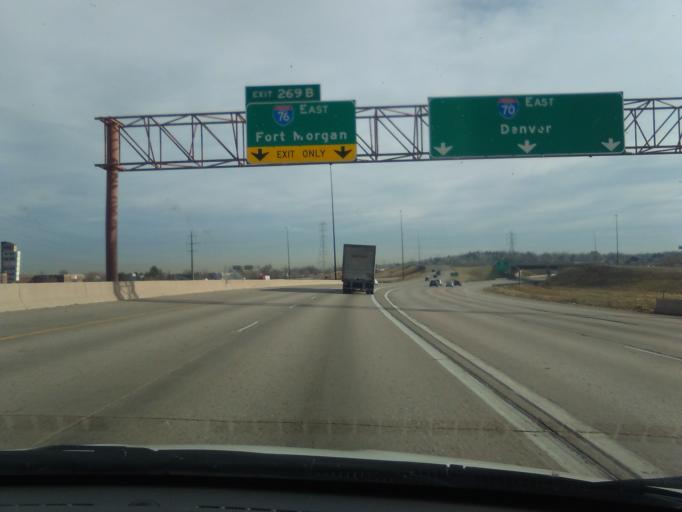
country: US
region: Colorado
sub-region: Jefferson County
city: Arvada
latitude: 39.7862
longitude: -105.0798
